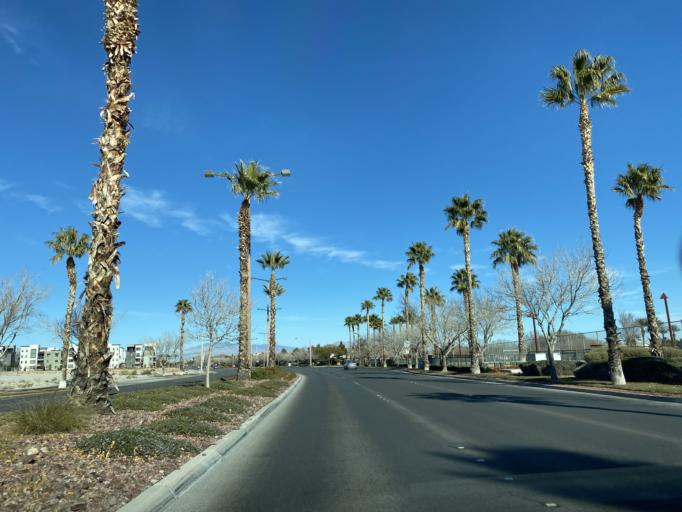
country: US
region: Nevada
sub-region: Clark County
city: Summerlin South
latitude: 36.1519
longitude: -115.3236
